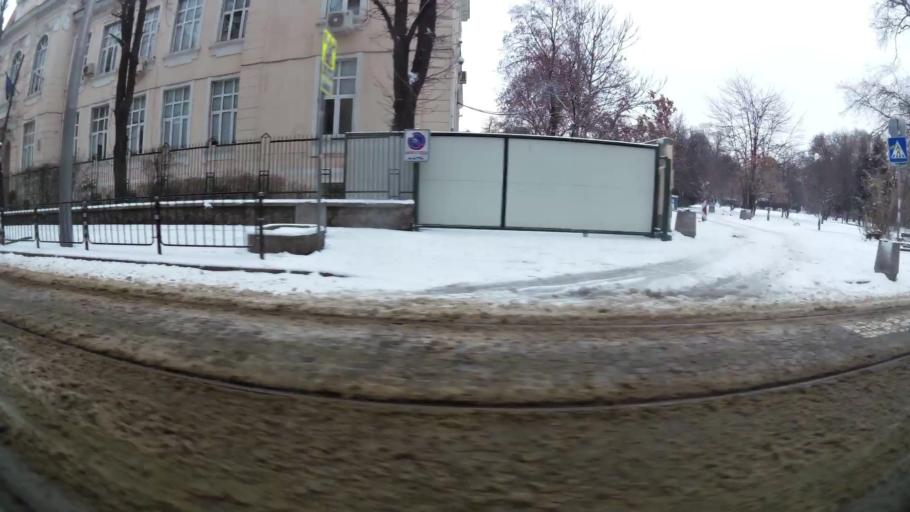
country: BG
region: Sofia-Capital
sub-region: Stolichna Obshtina
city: Sofia
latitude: 42.7016
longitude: 23.3085
